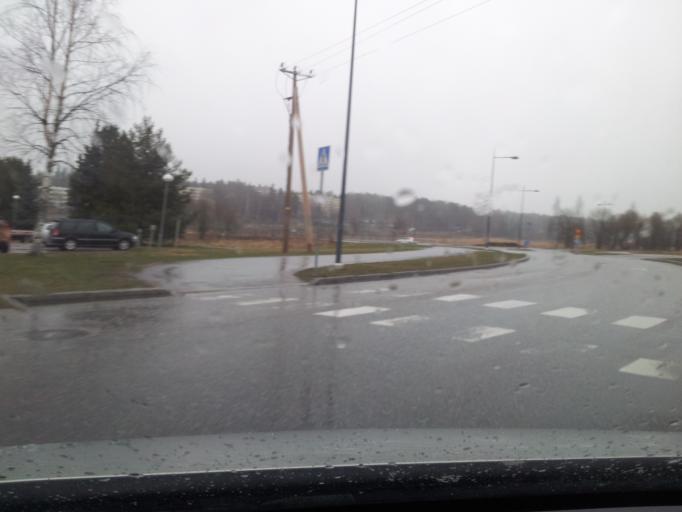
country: FI
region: Uusimaa
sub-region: Helsinki
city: Espoo
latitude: 60.1886
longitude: 24.6080
